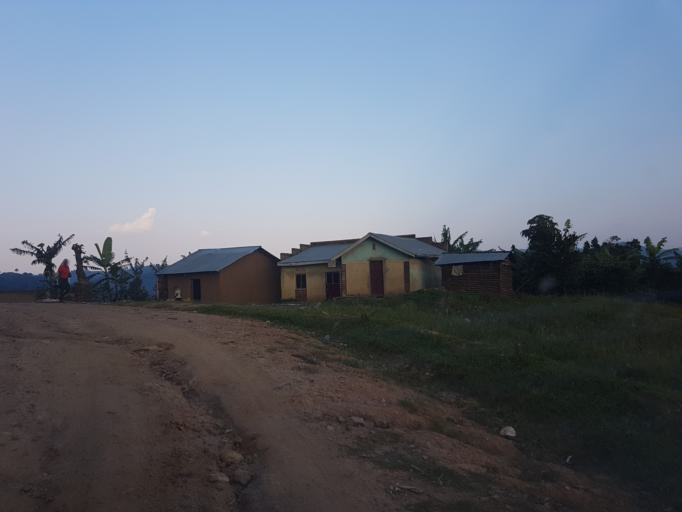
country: UG
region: Western Region
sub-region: Mitoma District
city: Mitoma
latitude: -0.6811
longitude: 29.9185
